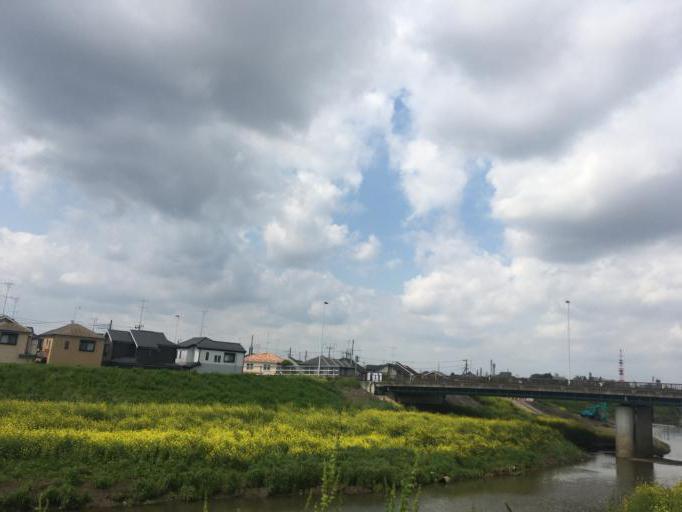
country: JP
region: Saitama
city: Kawagoe
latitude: 35.9000
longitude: 139.4979
